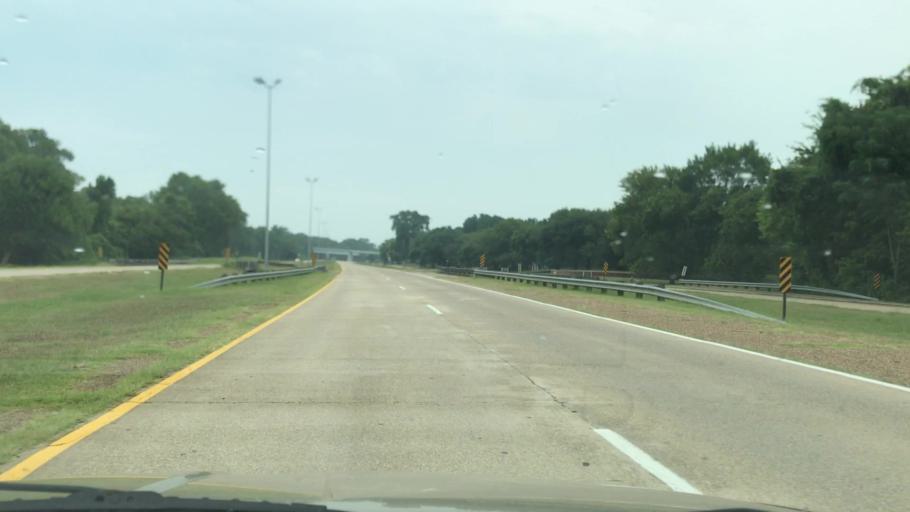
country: US
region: Louisiana
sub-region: Bossier Parish
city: Bossier City
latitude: 32.4957
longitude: -93.7092
